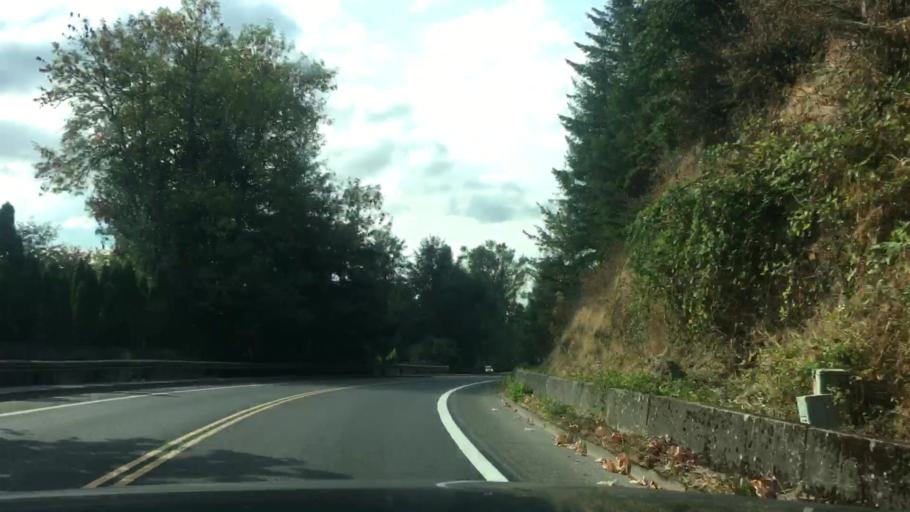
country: US
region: Oregon
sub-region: Lane County
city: Eugene
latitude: 44.0838
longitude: -123.0963
